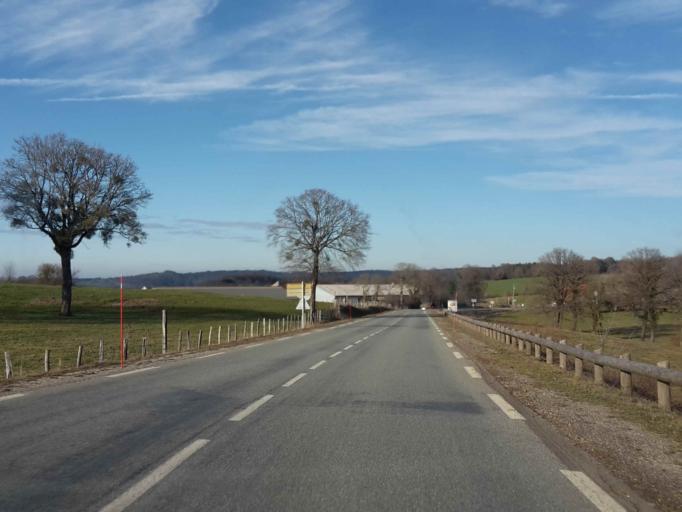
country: FR
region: Franche-Comte
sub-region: Departement du Doubs
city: Vercel-Villedieu-le-Camp
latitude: 47.2081
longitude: 6.3910
